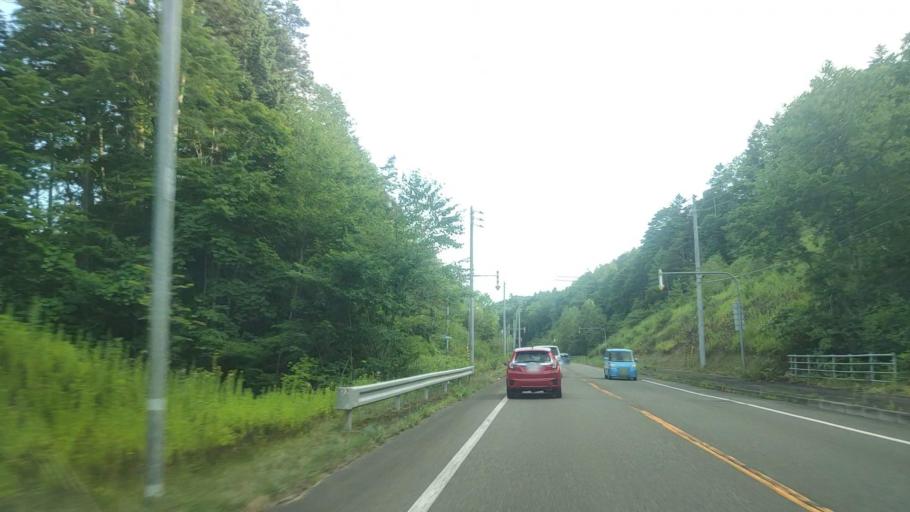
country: JP
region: Hokkaido
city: Iwamizawa
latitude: 43.0294
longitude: 141.9425
